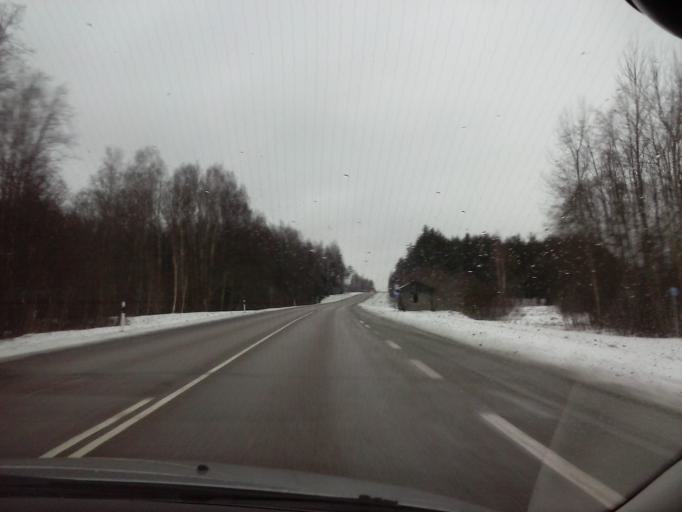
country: EE
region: Valgamaa
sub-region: Torva linn
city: Torva
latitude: 58.0558
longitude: 26.1942
